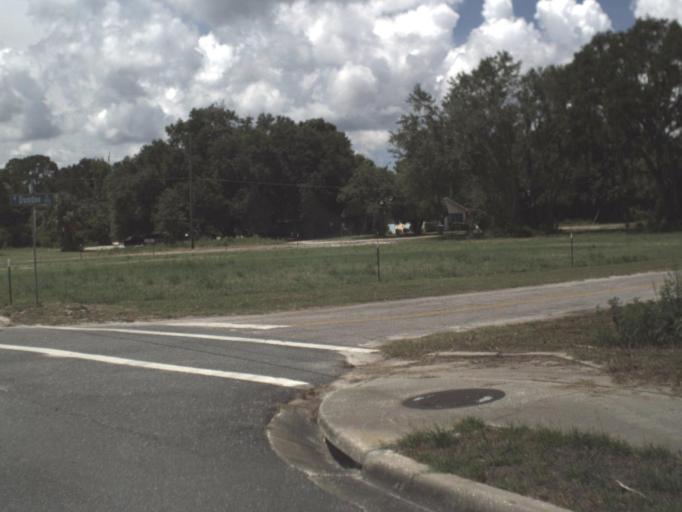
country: US
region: Florida
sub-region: Taylor County
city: Perry
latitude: 30.1102
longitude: -83.5893
